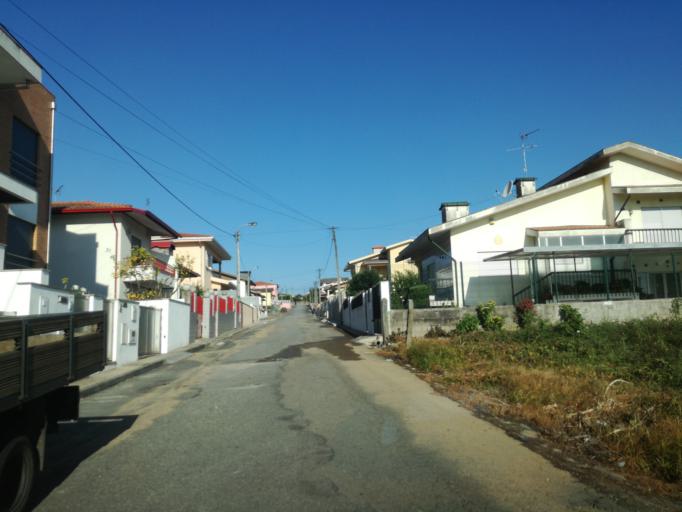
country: PT
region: Porto
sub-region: Trofa
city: Sao Romao do Coronado
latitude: 41.2630
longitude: -8.5718
